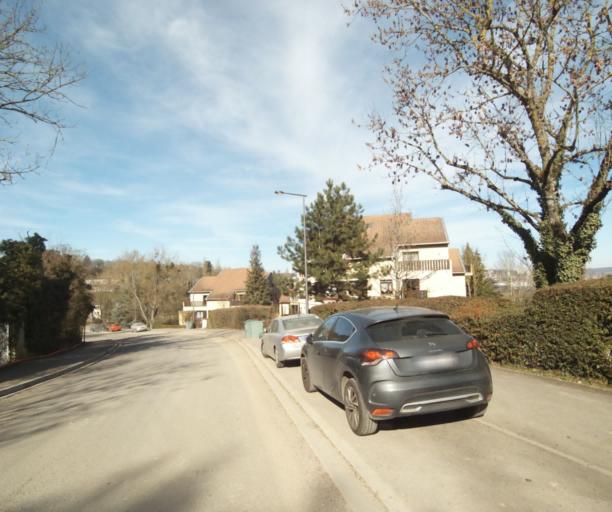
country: FR
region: Lorraine
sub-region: Departement de Meurthe-et-Moselle
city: Villers-les-Nancy
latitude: 48.6673
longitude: 6.1496
